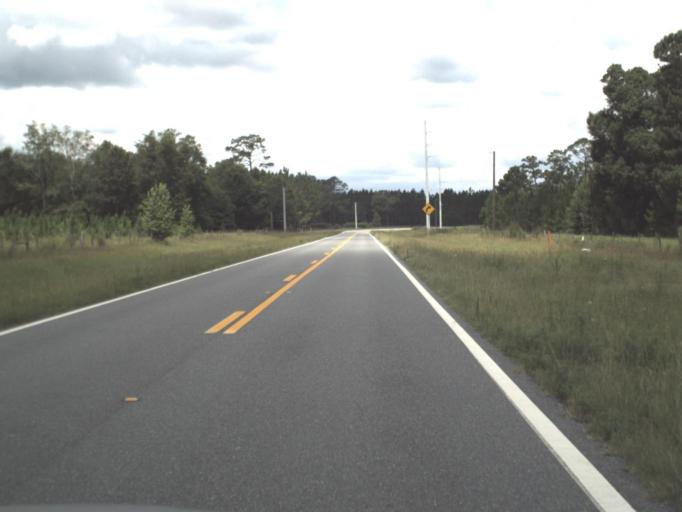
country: US
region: Florida
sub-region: Union County
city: Lake Butler
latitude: 29.9137
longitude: -82.3950
